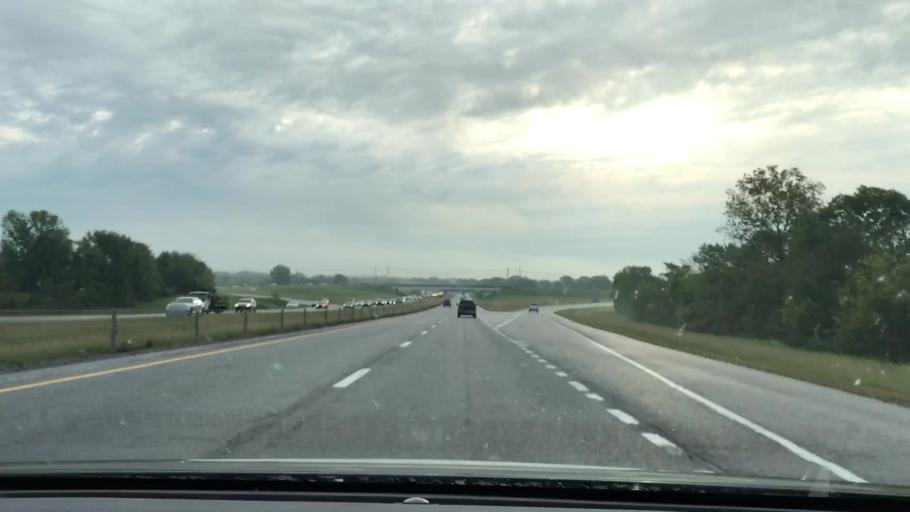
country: US
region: Tennessee
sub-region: Sumner County
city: Hendersonville
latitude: 36.3306
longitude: -86.6253
